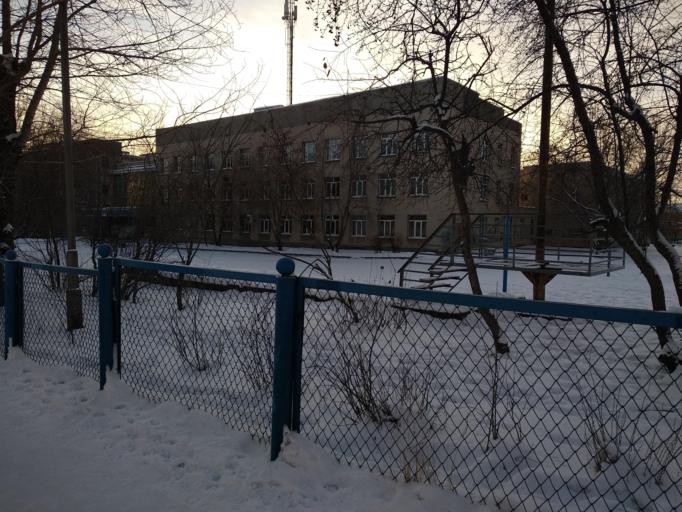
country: RU
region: Sverdlovsk
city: Krasnotur'insk
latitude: 59.7627
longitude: 60.2066
